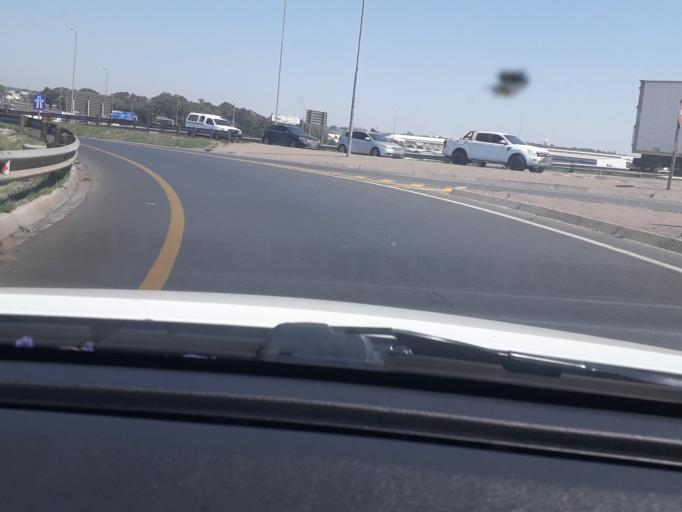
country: ZA
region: Gauteng
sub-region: Ekurhuleni Metropolitan Municipality
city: Boksburg
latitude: -26.1743
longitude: 28.2419
